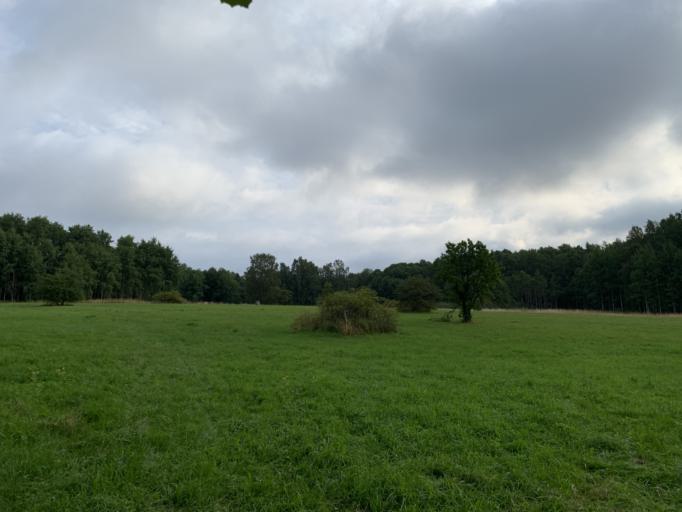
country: SE
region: Stockholm
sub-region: Stockholms Kommun
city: Kista
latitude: 59.3954
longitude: 17.9727
